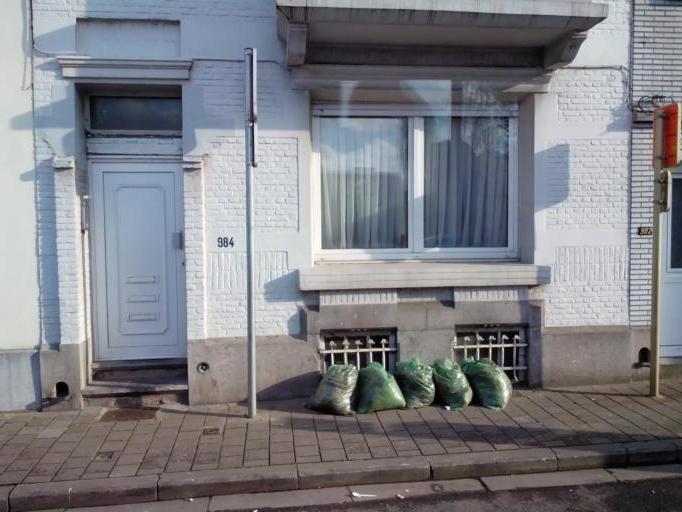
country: BE
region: Flanders
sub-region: Provincie Vlaams-Brabant
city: Diegem
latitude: 50.8598
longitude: 4.4175
